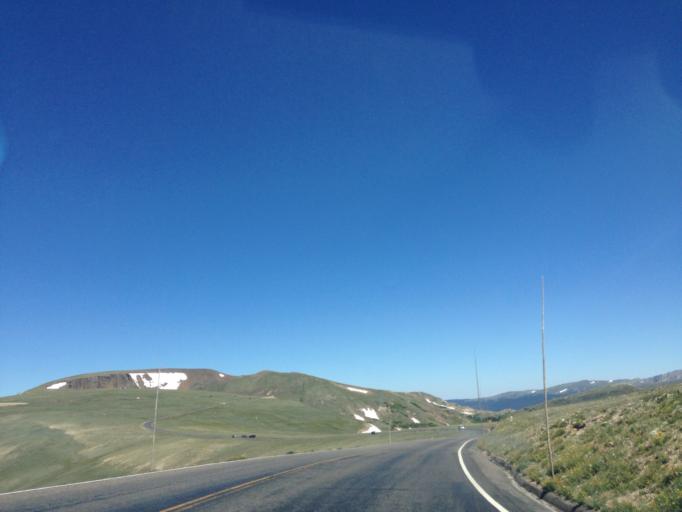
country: US
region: Colorado
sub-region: Larimer County
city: Estes Park
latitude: 40.4136
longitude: -105.7450
